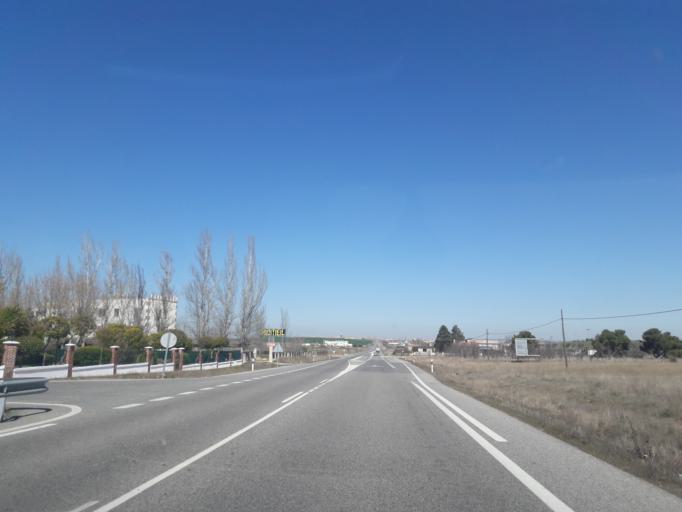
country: ES
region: Castille and Leon
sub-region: Provincia de Salamanca
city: Miranda de Azan
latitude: 40.8935
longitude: -5.6643
